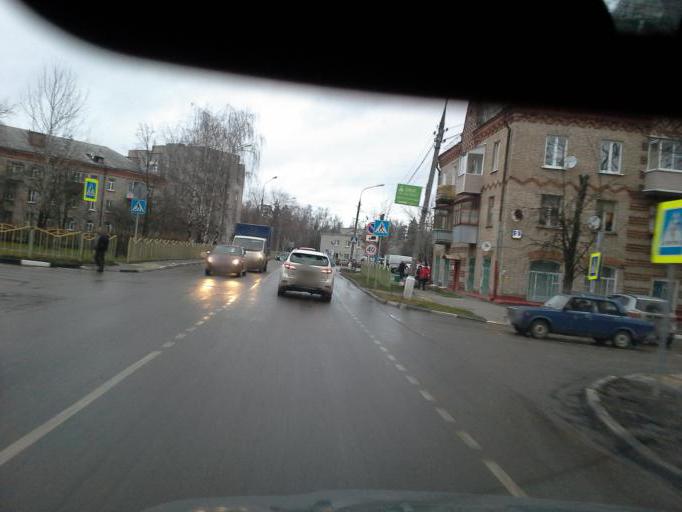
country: RU
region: Moskovskaya
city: Kokoshkino
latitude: 55.6003
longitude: 37.1652
